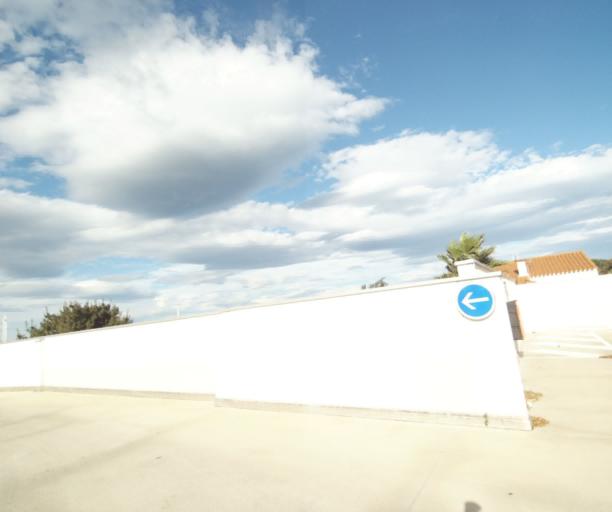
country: FR
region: Languedoc-Roussillon
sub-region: Departement des Pyrenees-Orientales
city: Argelers
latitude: 42.5457
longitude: 3.0312
